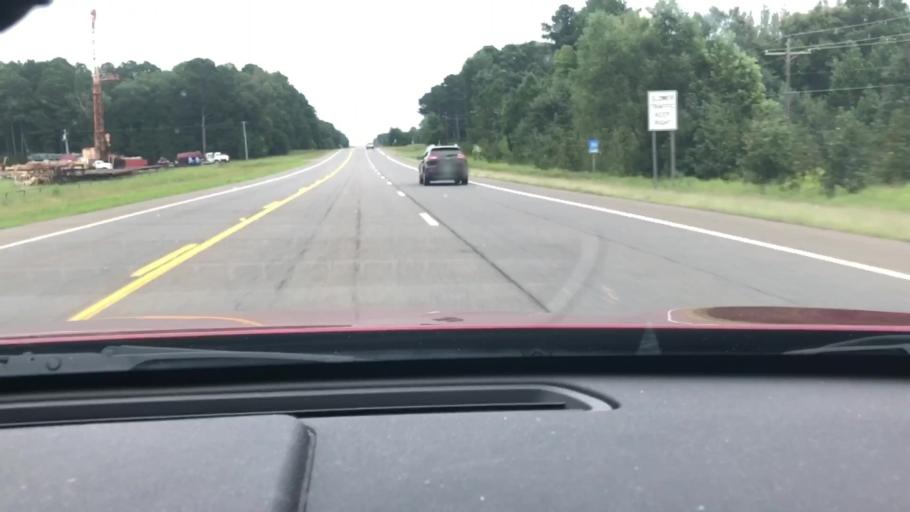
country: US
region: Arkansas
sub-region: Lafayette County
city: Stamps
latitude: 33.3642
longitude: -93.4715
